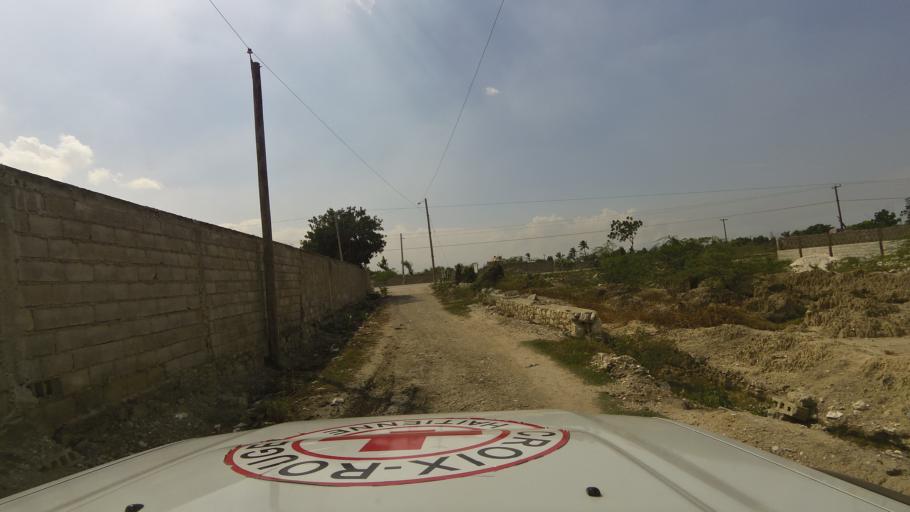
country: HT
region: Ouest
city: Croix des Bouquets
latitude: 18.6415
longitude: -72.2713
